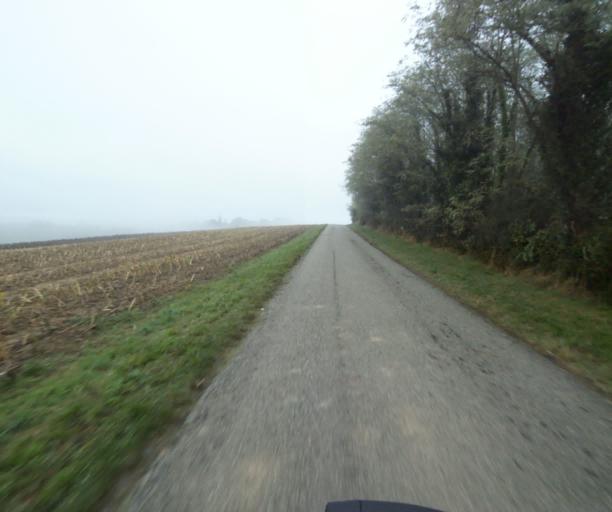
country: FR
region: Midi-Pyrenees
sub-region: Departement du Tarn-et-Garonne
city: Saint-Nauphary
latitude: 43.9444
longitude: 1.4096
